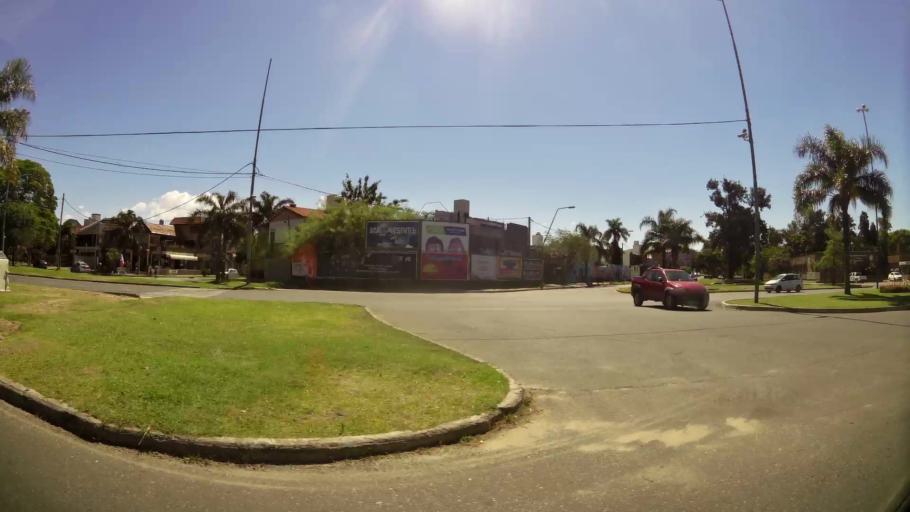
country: AR
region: Santa Fe
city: Santa Fe de la Vera Cruz
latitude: -31.6297
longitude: -60.6781
